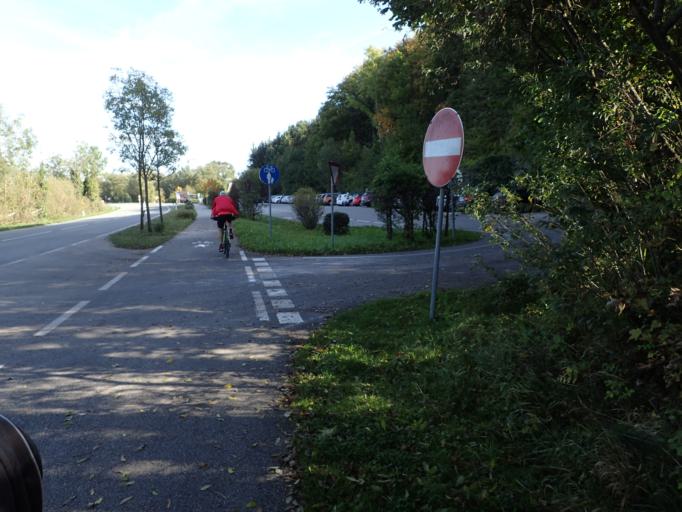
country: AT
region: Salzburg
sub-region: Politischer Bezirk Salzburg-Umgebung
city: Mattsee
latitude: 47.9755
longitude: 13.1036
